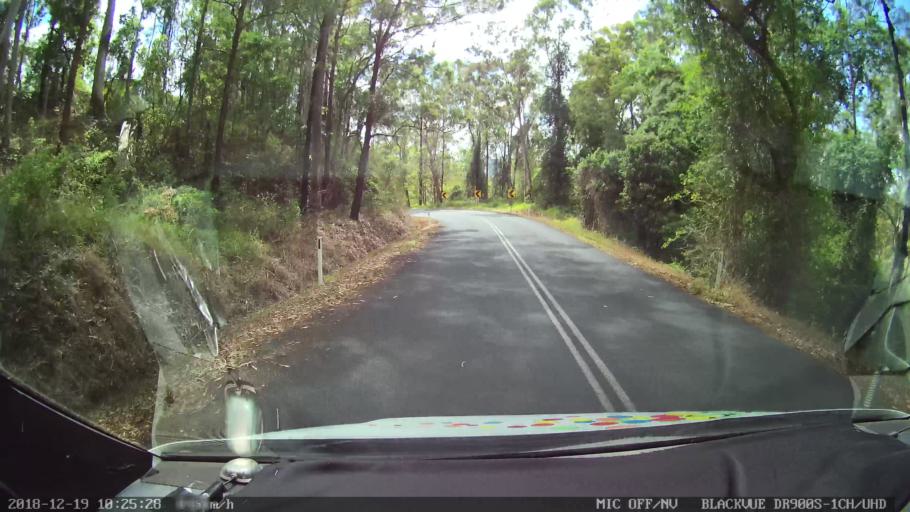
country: AU
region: New South Wales
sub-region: Lismore Municipality
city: Larnook
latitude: -28.5936
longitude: 153.0850
